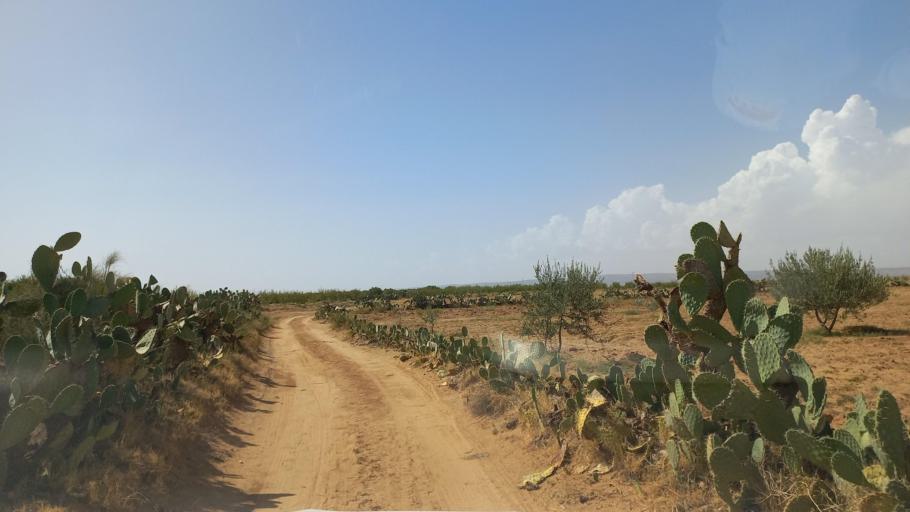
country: TN
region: Al Qasrayn
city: Kasserine
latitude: 35.2111
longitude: 9.0356
